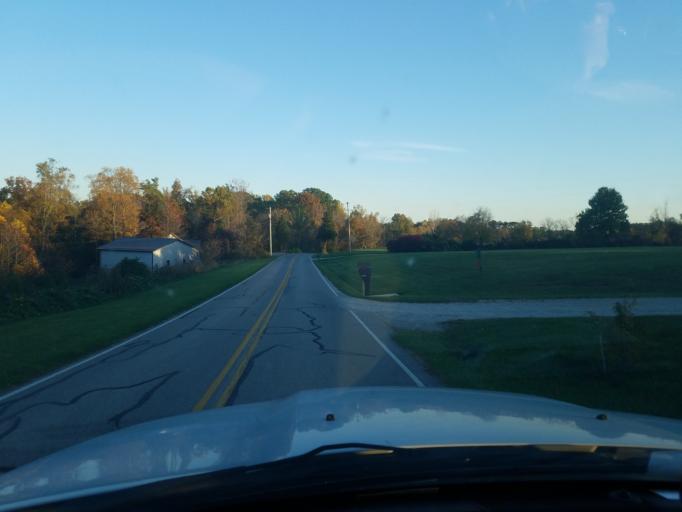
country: US
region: Indiana
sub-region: Floyd County
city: Galena
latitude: 38.3793
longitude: -85.9031
